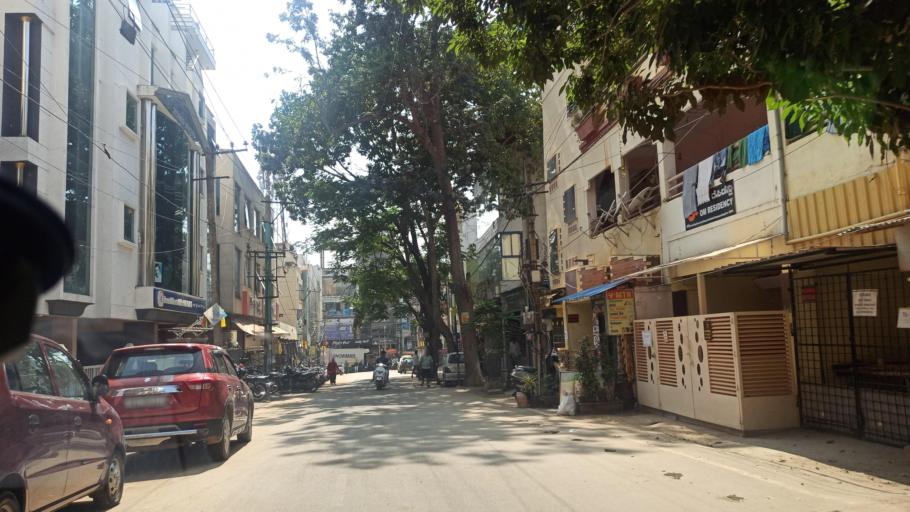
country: IN
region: Karnataka
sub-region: Bangalore Urban
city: Yelahanka
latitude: 13.0511
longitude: 77.5976
